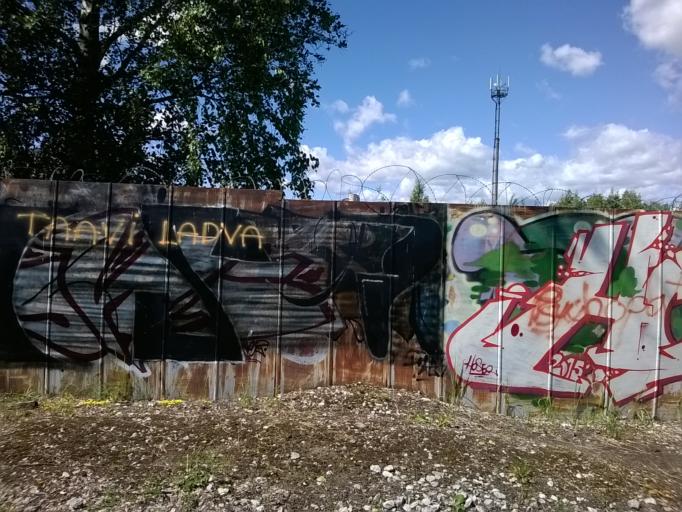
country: EE
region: Tartu
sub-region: Tartu linn
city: Tartu
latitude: 58.3636
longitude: 26.7474
